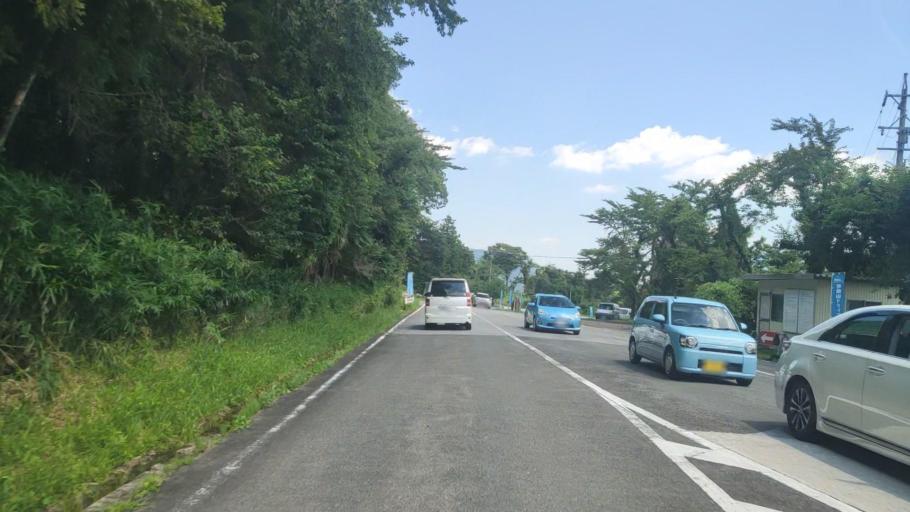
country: JP
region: Gifu
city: Tarui
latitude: 35.3745
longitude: 136.4486
